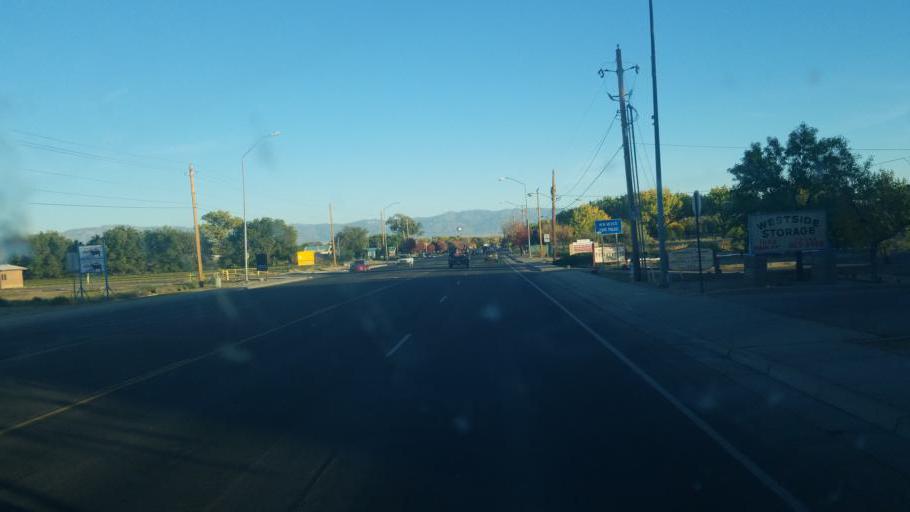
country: US
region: New Mexico
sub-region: Valencia County
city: Los Lunas
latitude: 34.8134
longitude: -106.7454
